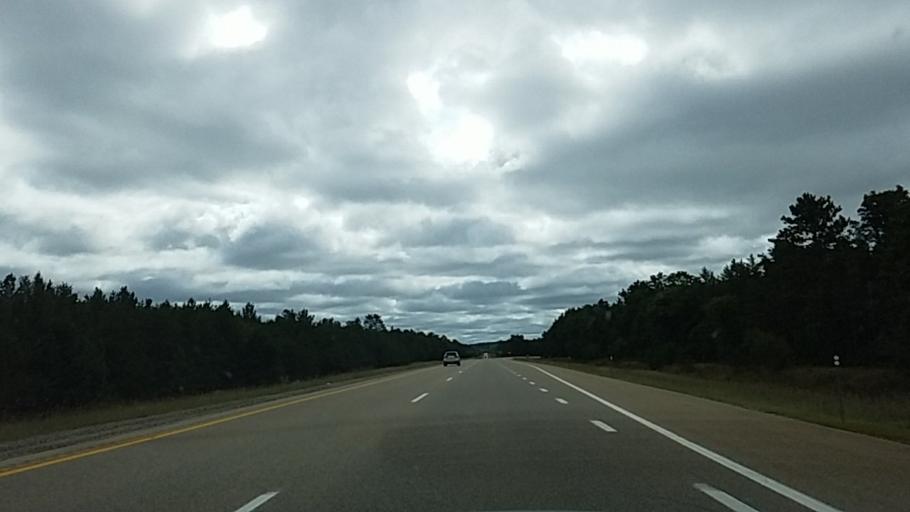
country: US
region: Michigan
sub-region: Roscommon County
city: Roscommon
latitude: 44.5183
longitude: -84.6673
